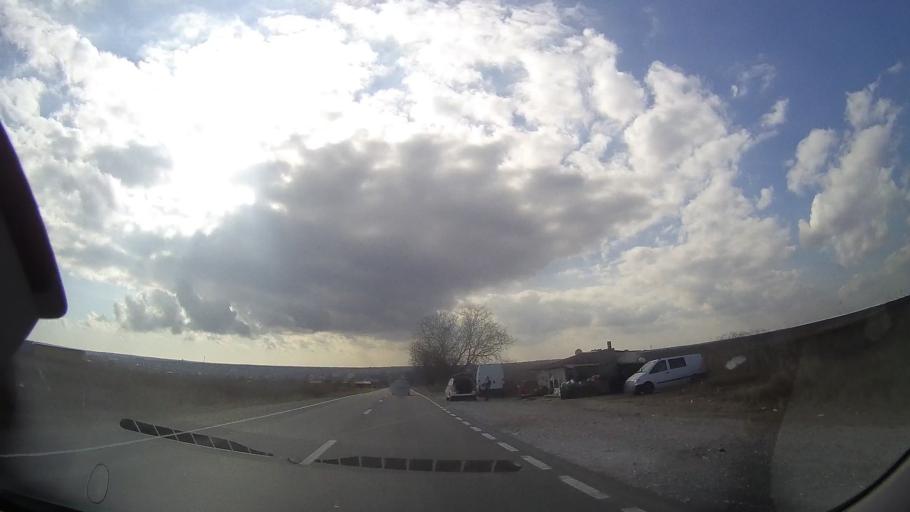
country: RO
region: Constanta
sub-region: Oras Techirghiol
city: Techirghiol
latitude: 44.0698
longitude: 28.5958
